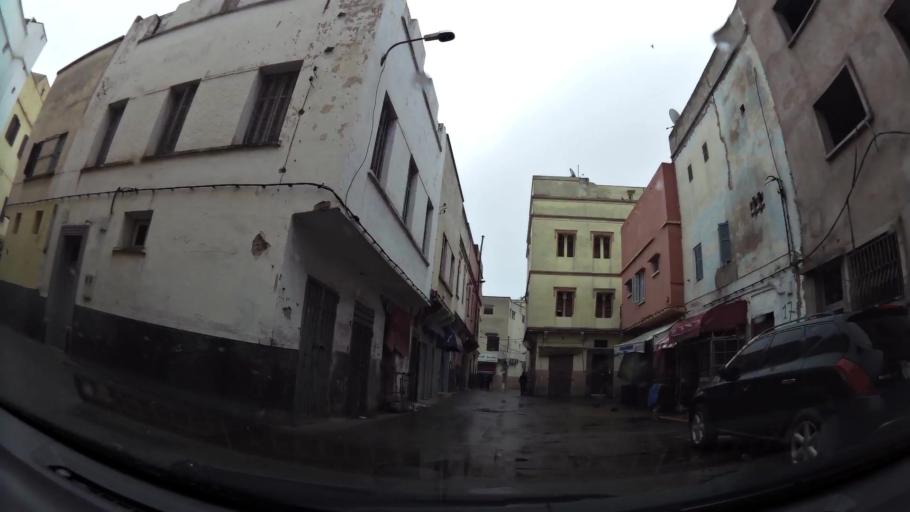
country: MA
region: Grand Casablanca
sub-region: Casablanca
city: Casablanca
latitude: 33.5775
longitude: -7.6085
